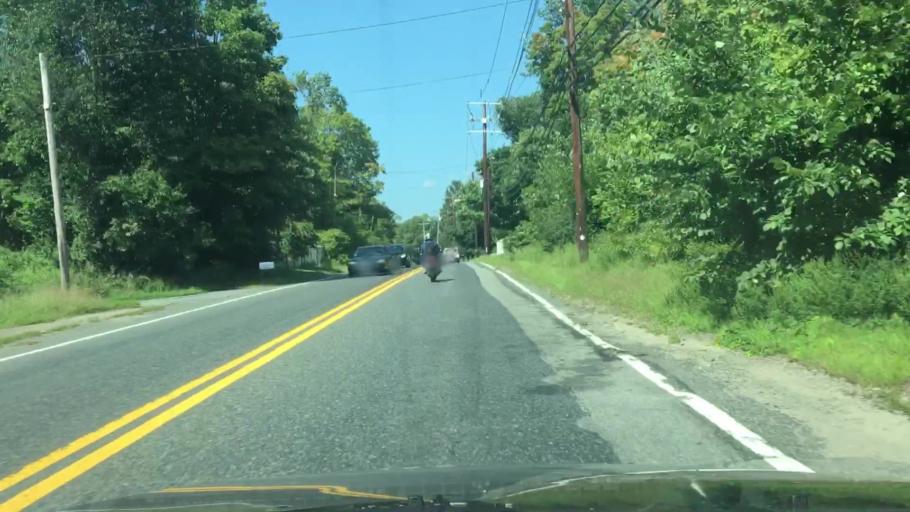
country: US
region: Massachusetts
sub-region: Middlesex County
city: Holliston
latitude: 42.1865
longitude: -71.4401
